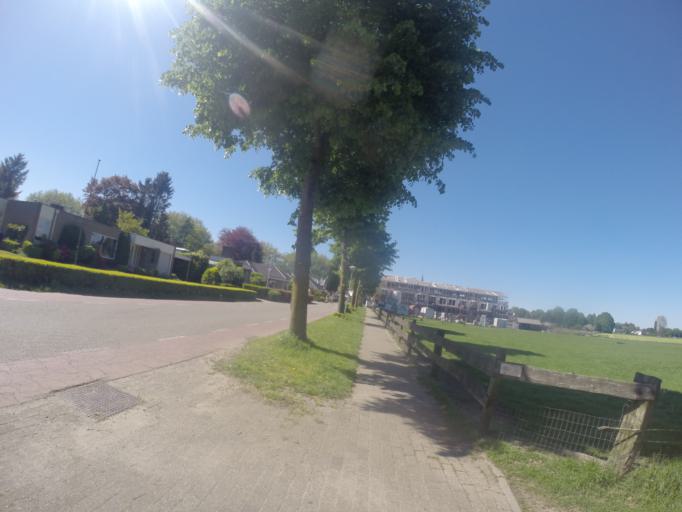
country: NL
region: Gelderland
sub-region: Gemeente Montferland
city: s-Heerenberg
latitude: 51.9050
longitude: 6.1928
